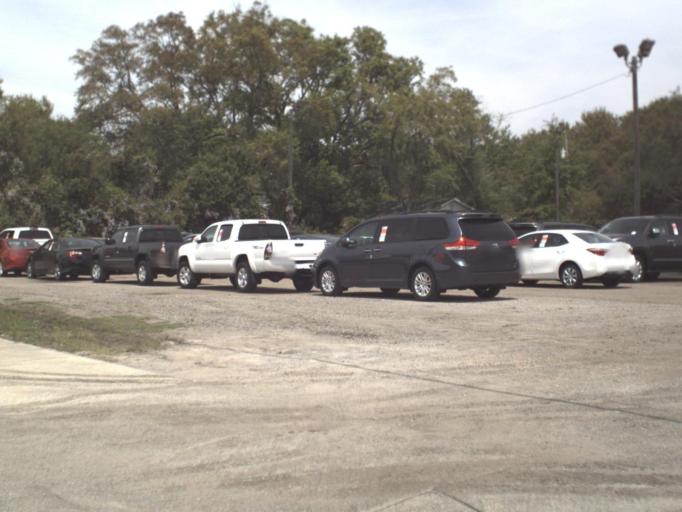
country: US
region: Florida
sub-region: Okaloosa County
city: Wright
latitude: 30.4536
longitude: -86.6384
